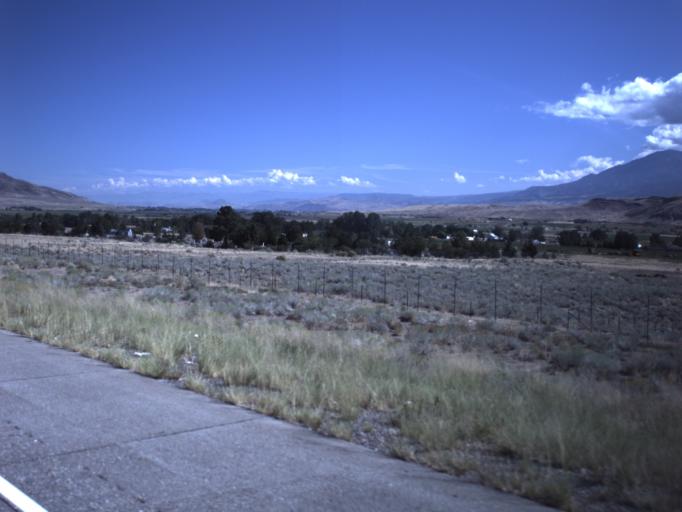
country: US
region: Utah
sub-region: Sevier County
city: Monroe
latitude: 38.6173
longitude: -112.2290
